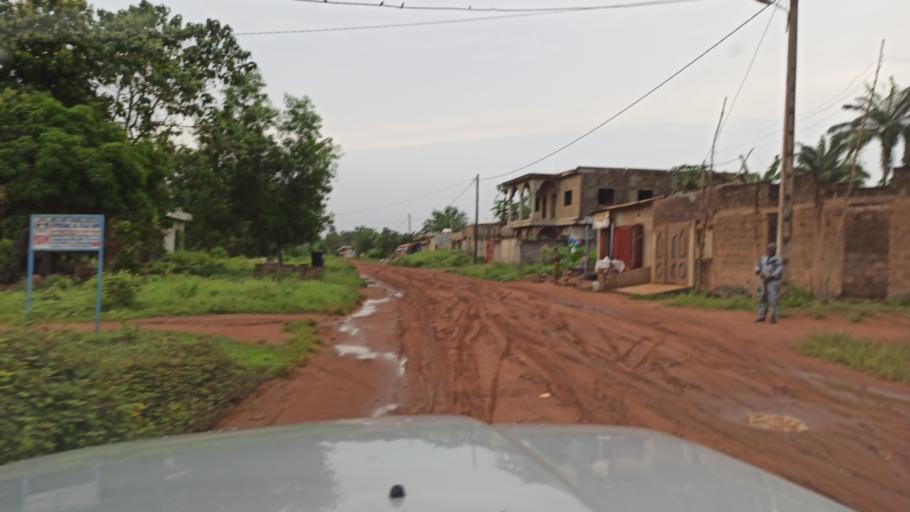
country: BJ
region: Queme
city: Porto-Novo
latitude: 6.4826
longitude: 2.6719
